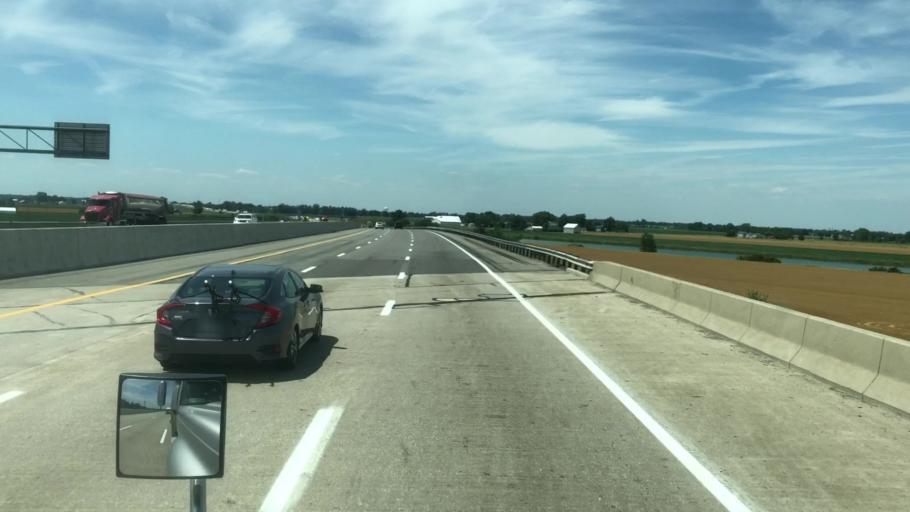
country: US
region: Ohio
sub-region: Wood County
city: Walbridge
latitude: 41.5342
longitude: -83.4833
